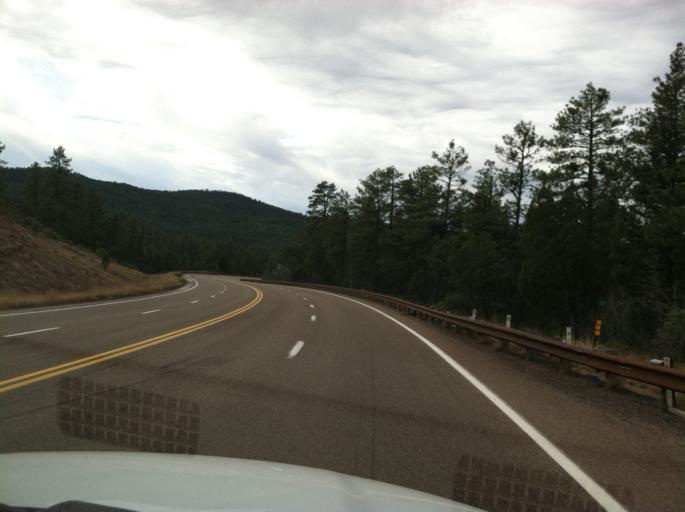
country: US
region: Arizona
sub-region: Gila County
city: Star Valley
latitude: 34.2999
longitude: -110.9620
